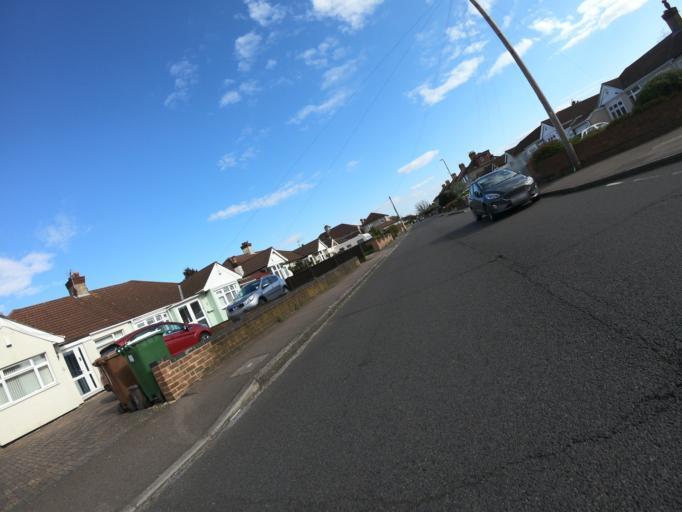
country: GB
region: England
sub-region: Greater London
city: Bexleyheath
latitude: 51.4738
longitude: 0.1348
